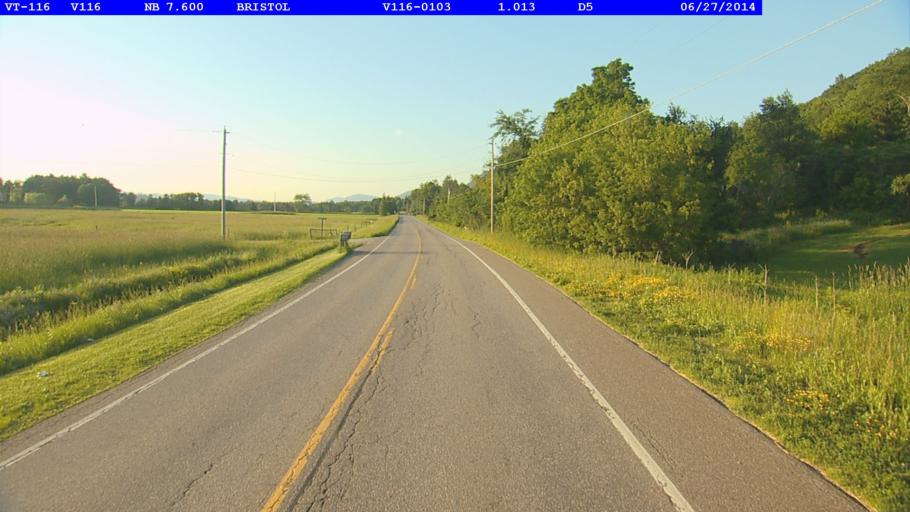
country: US
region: Vermont
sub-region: Addison County
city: Bristol
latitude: 44.0683
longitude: -73.0864
